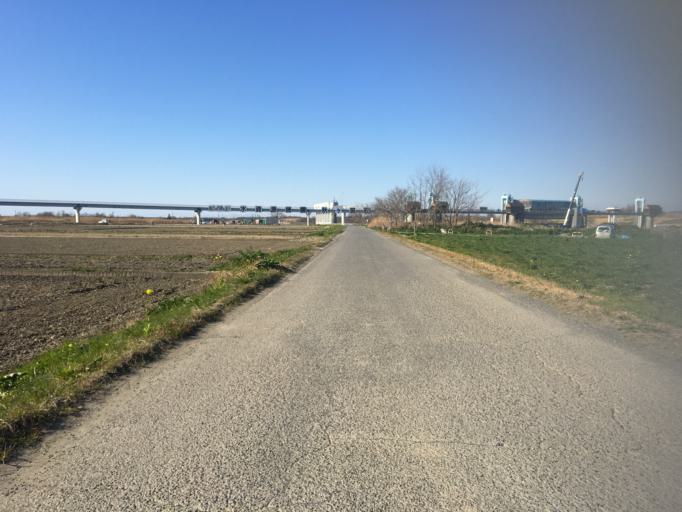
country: JP
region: Saitama
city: Shiki
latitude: 35.8380
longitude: 139.6043
